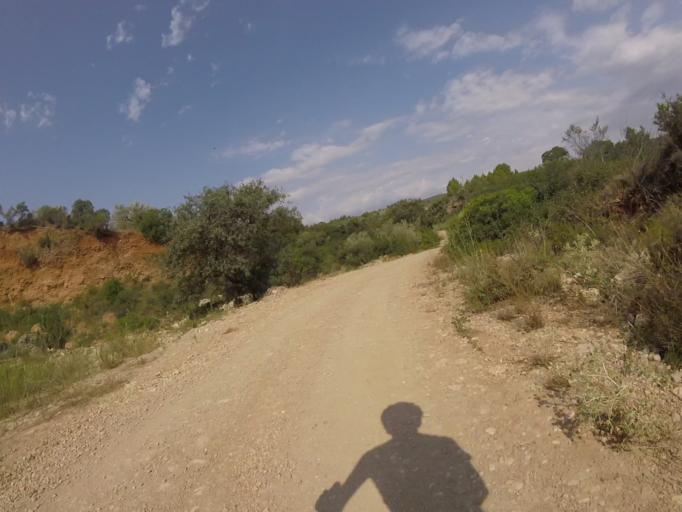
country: ES
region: Valencia
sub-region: Provincia de Castello
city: Alcala de Xivert
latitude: 40.3166
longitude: 0.1859
